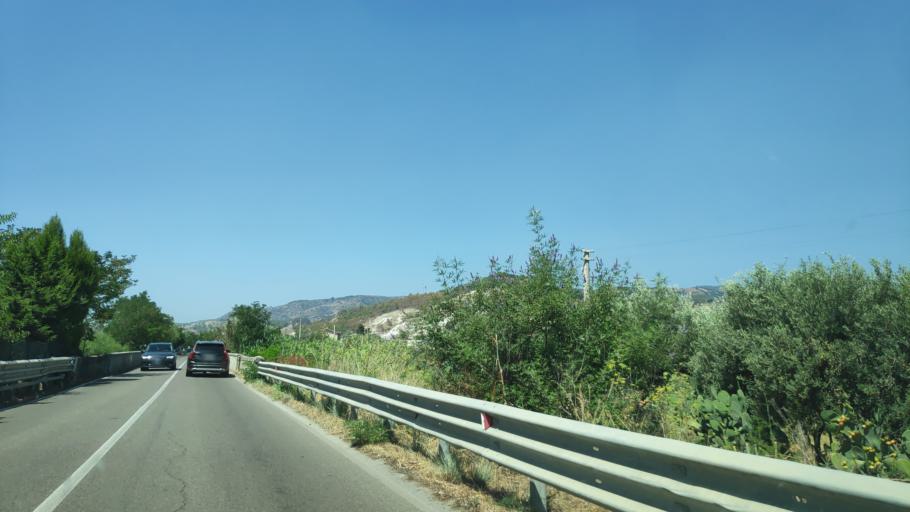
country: IT
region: Calabria
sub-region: Provincia di Reggio Calabria
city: Palizzi Marina
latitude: 37.9231
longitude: 16.0446
